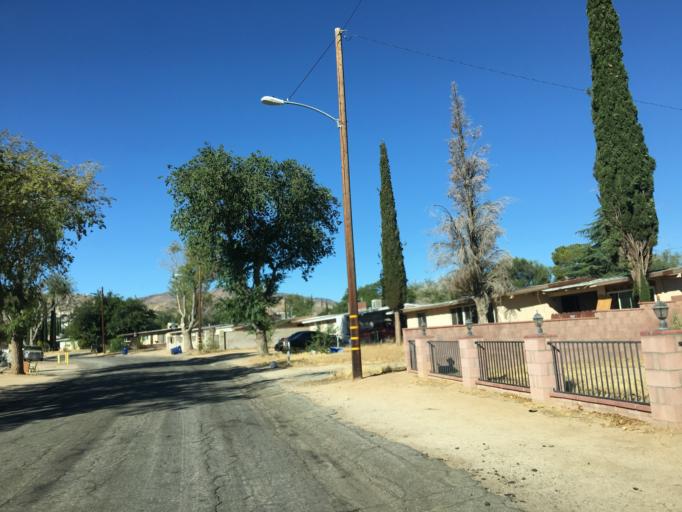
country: US
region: California
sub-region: Los Angeles County
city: Desert View Highlands
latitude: 34.5895
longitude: -118.1520
